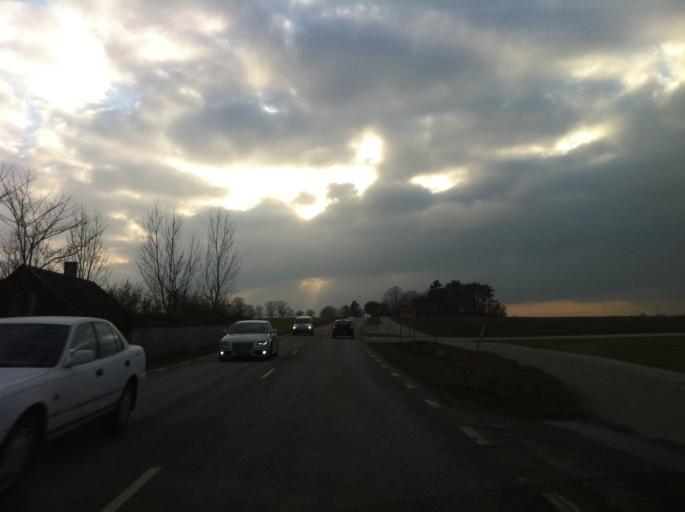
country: SE
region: Skane
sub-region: Kavlinge Kommun
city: Kaevlinge
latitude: 55.7829
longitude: 13.0734
